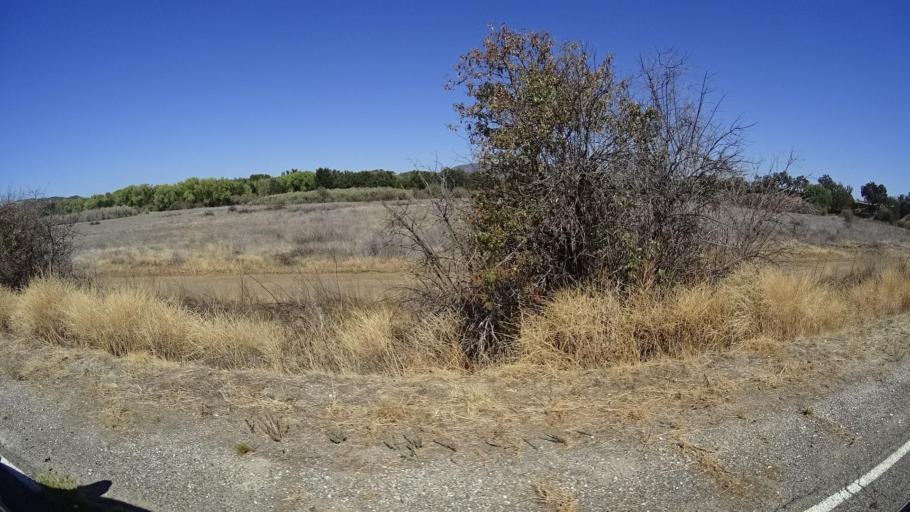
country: US
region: California
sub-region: San Luis Obispo County
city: Lake Nacimiento
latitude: 35.8855
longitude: -121.0678
